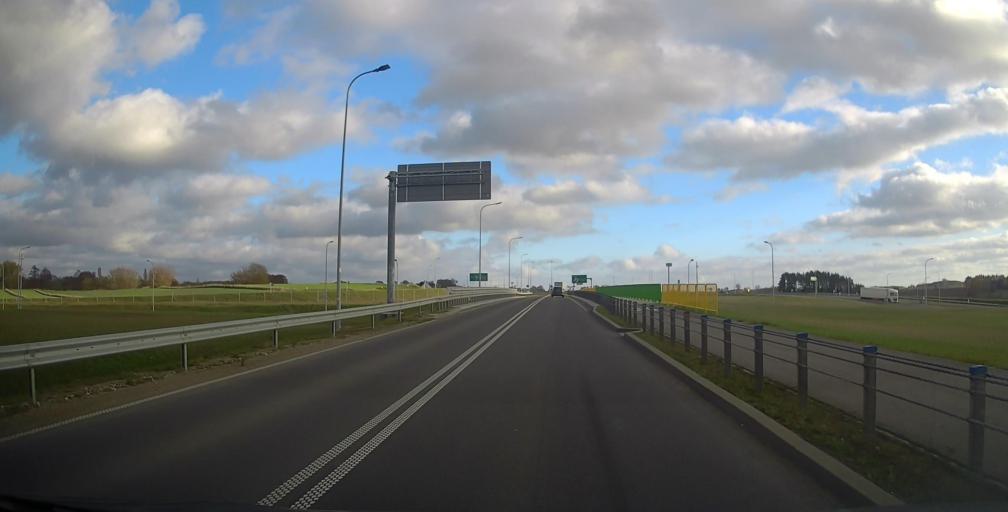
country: PL
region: Podlasie
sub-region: Powiat lomzynski
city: Piatnica
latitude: 53.2503
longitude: 22.1048
